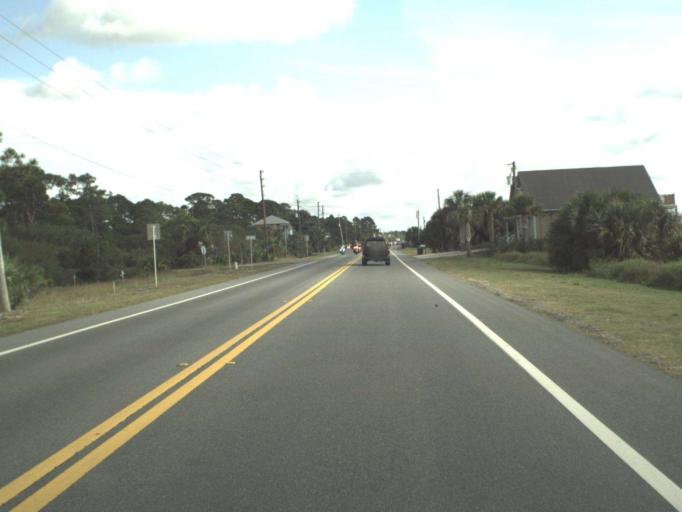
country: US
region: Florida
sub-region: Bay County
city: Mexico Beach
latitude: 29.9067
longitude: -85.3700
